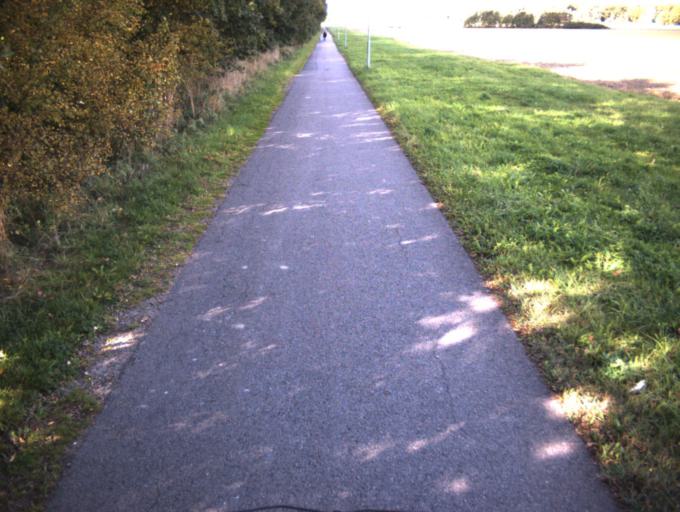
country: SE
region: Skane
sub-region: Helsingborg
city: Helsingborg
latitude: 56.0848
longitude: 12.6752
